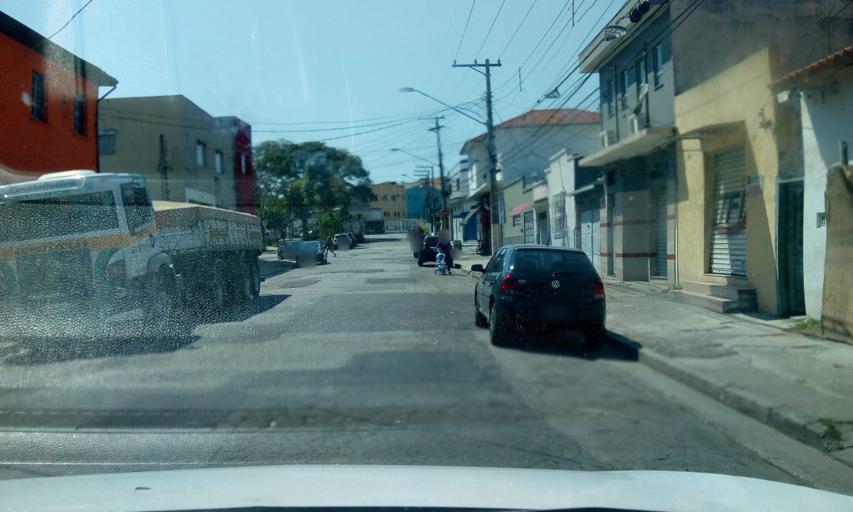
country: BR
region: Sao Paulo
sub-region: Osasco
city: Osasco
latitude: -23.5158
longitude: -46.7205
